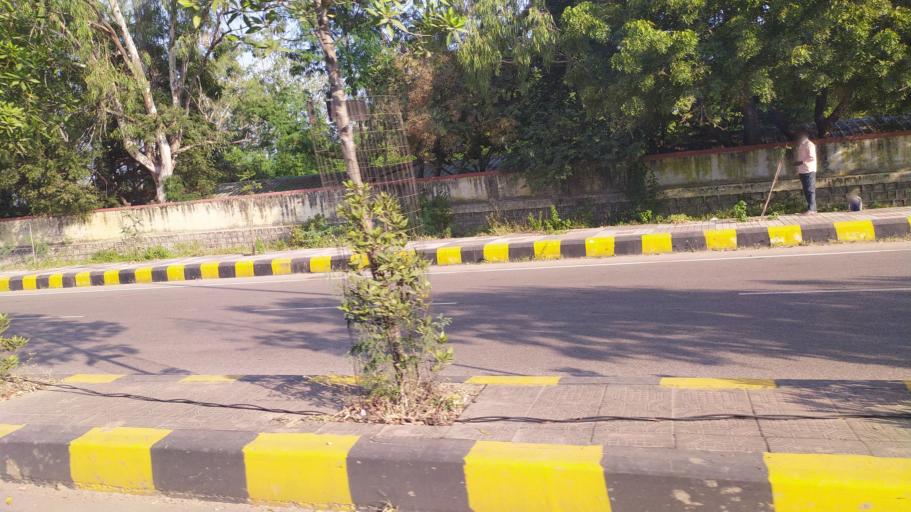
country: IN
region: Telangana
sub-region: Hyderabad
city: Hyderabad
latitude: 17.3196
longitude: 78.3926
